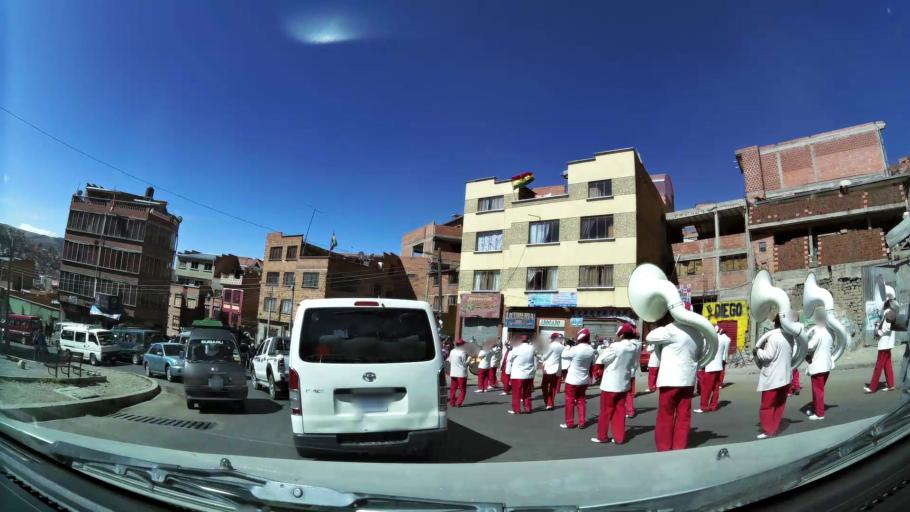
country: BO
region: La Paz
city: La Paz
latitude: -16.4937
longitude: -68.1639
